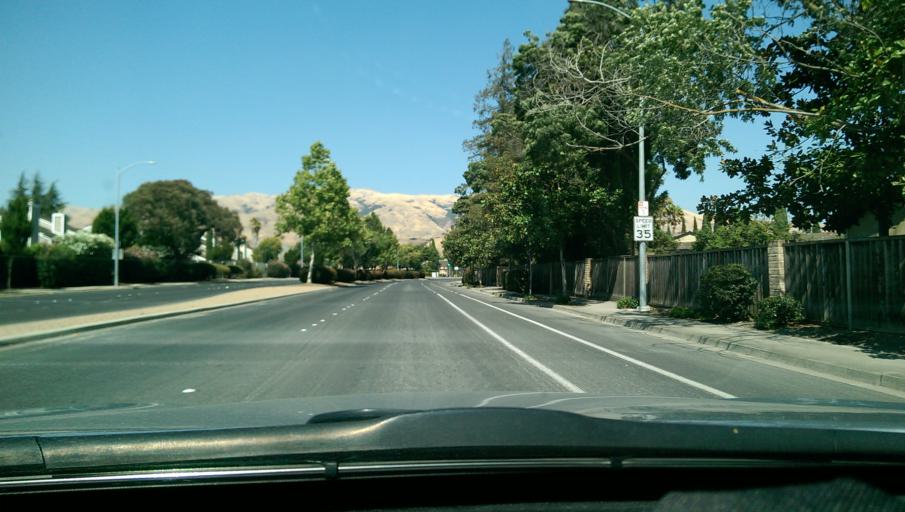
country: US
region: California
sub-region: Santa Clara County
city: Milpitas
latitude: 37.4449
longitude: -121.9063
